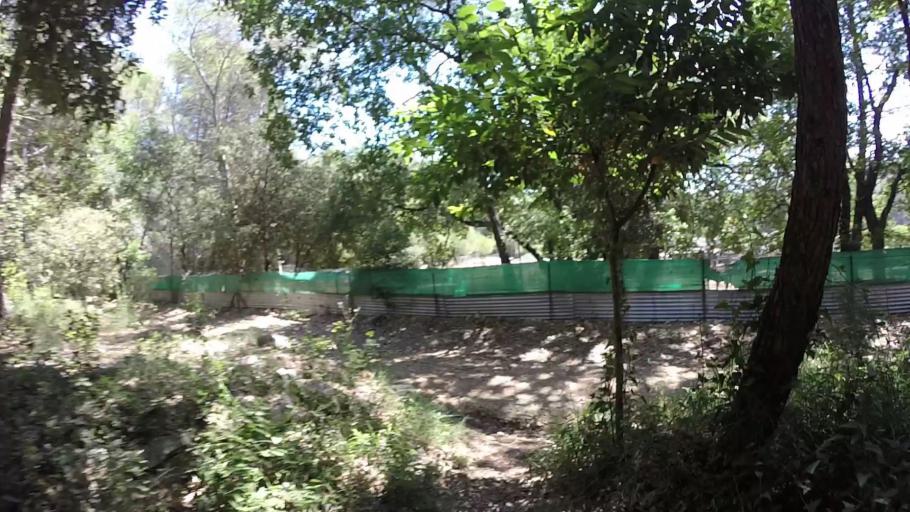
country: FR
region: Provence-Alpes-Cote d'Azur
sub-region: Departement des Alpes-Maritimes
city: Vallauris
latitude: 43.5972
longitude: 7.0438
